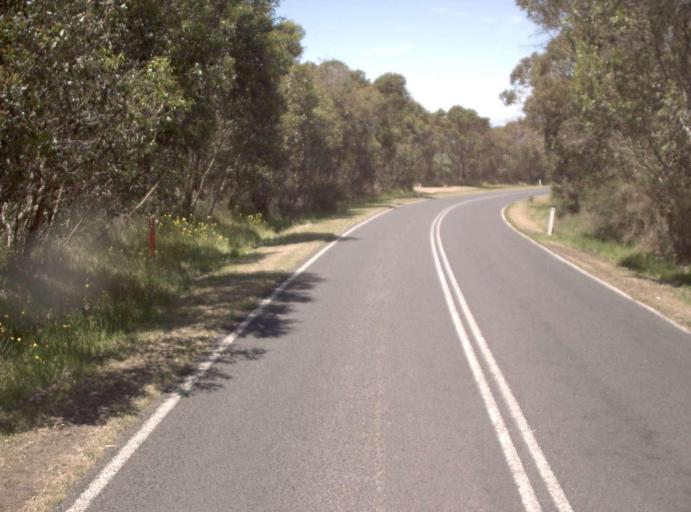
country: AU
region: Victoria
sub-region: Bass Coast
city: North Wonthaggi
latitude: -38.7458
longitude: 146.1332
